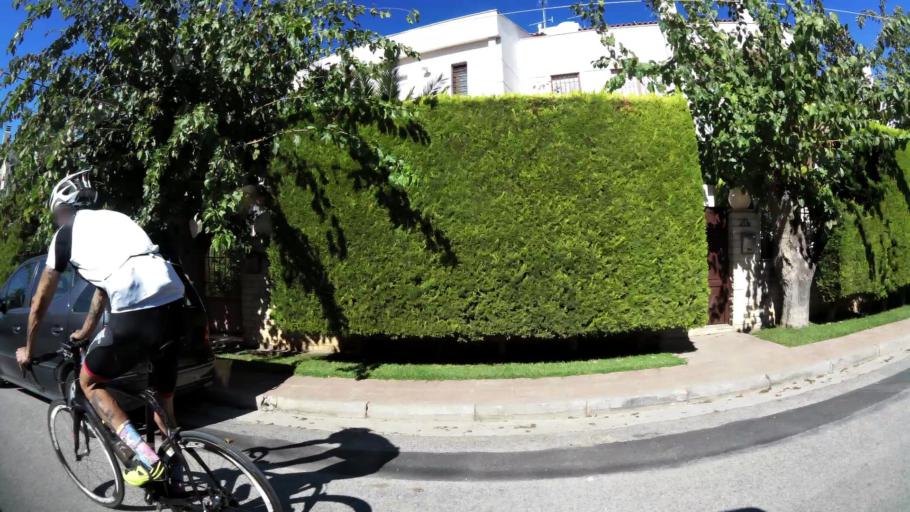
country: GR
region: Attica
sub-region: Nomarchia Athinas
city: Nea Erythraia
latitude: 38.1025
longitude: 23.8220
